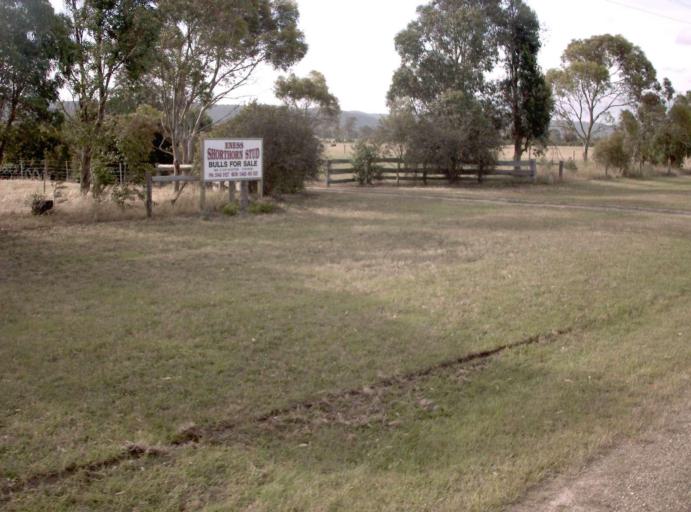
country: AU
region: Victoria
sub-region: Wellington
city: Heyfield
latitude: -38.0400
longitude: 146.6660
